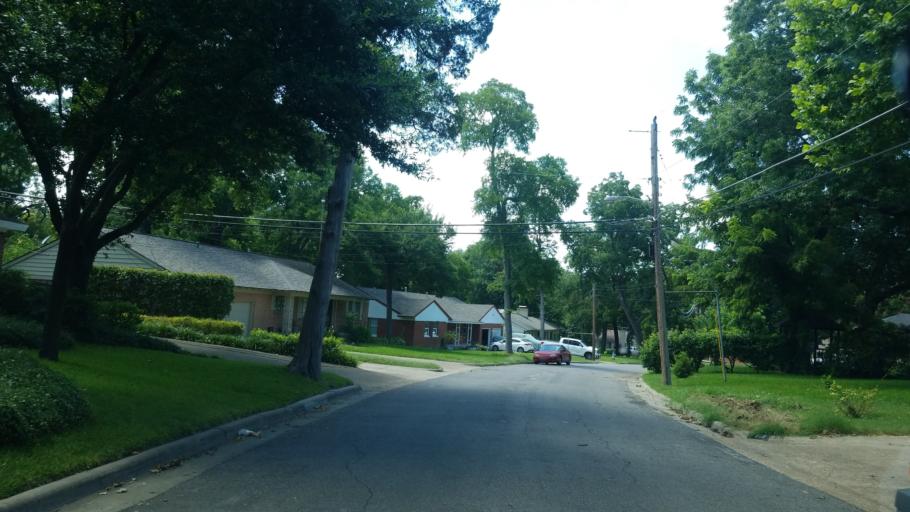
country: US
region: Texas
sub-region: Dallas County
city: Balch Springs
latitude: 32.7553
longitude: -96.6983
